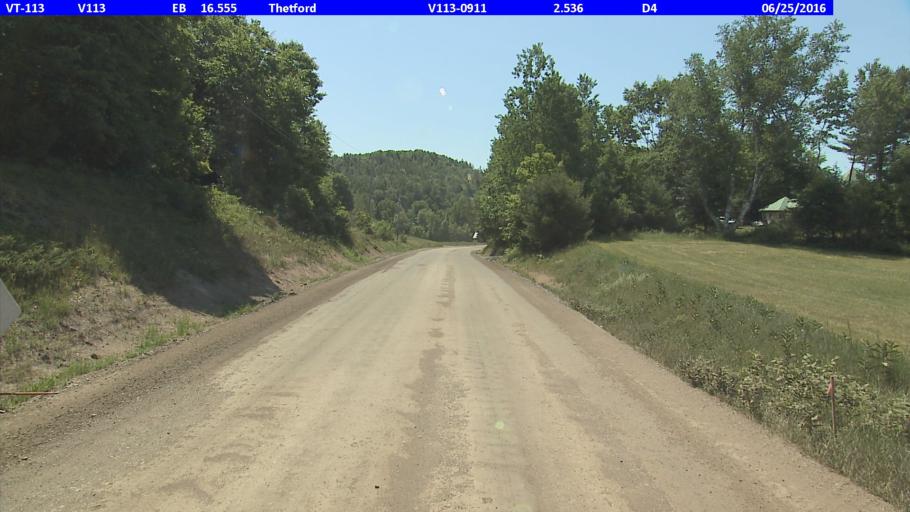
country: US
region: New Hampshire
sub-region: Grafton County
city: Lyme
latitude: 43.8623
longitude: -72.2607
